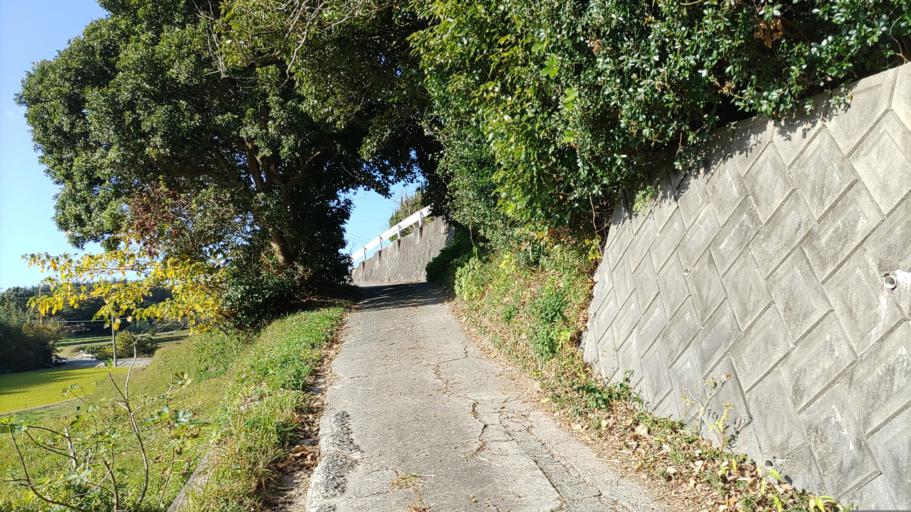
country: JP
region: Hyogo
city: Sumoto
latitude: 34.3898
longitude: 134.8140
